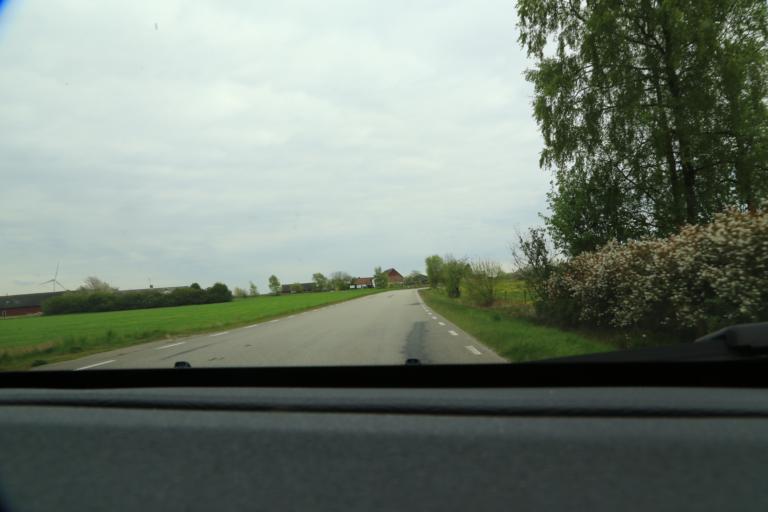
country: SE
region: Halland
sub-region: Varbergs Kommun
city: Tvaaker
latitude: 57.0445
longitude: 12.3635
